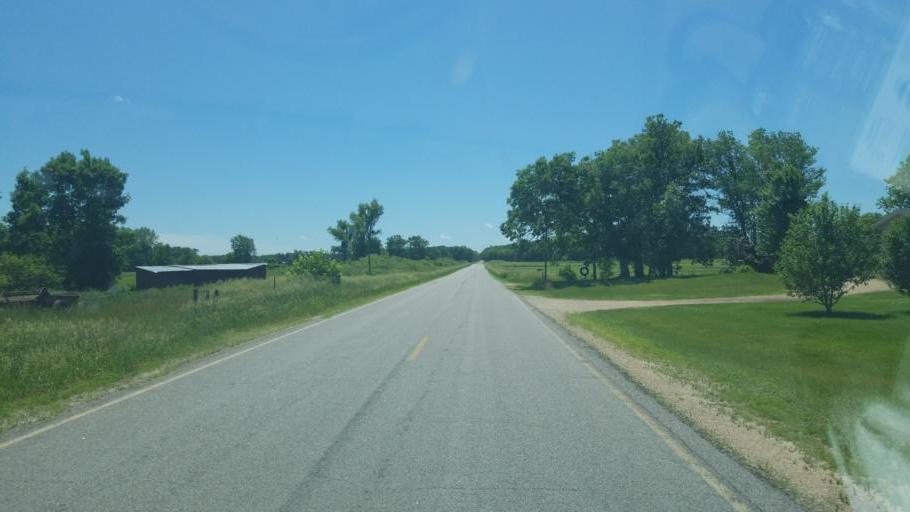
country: US
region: Wisconsin
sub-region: Juneau County
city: New Lisbon
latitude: 44.0028
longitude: -90.2718
